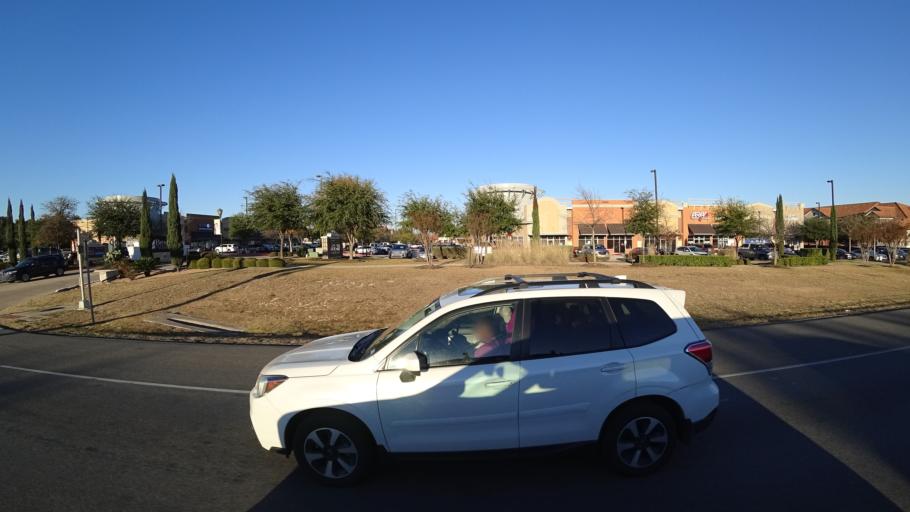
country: US
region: Texas
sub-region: Williamson County
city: Brushy Creek
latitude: 30.5310
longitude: -97.7801
